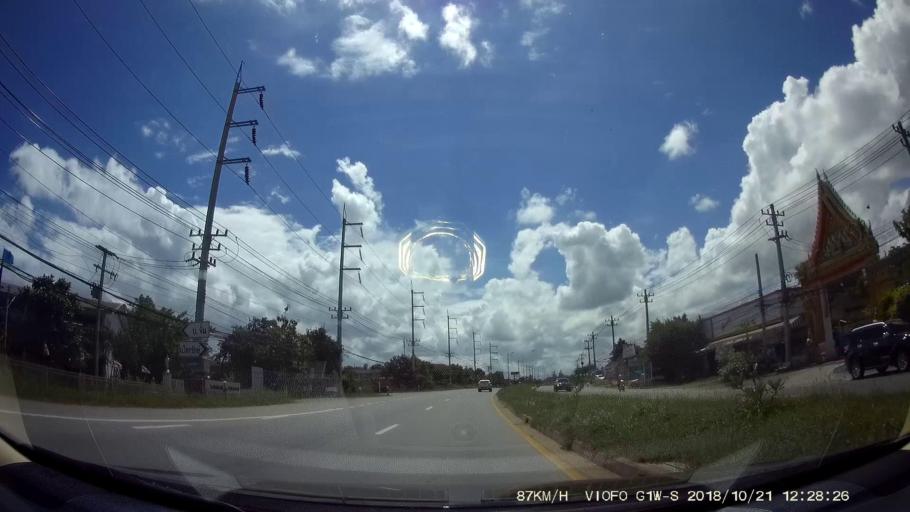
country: TH
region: Nakhon Ratchasima
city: Dan Khun Thot
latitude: 15.1894
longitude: 101.7605
